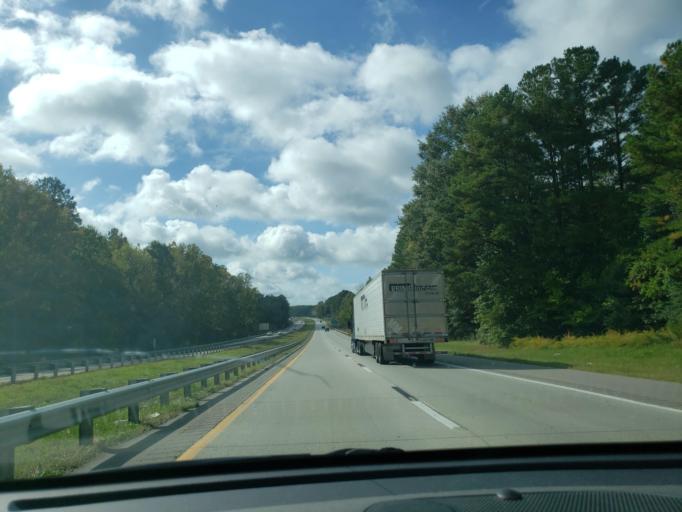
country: US
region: North Carolina
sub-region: Vance County
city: Henderson
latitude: 36.3394
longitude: -78.4158
